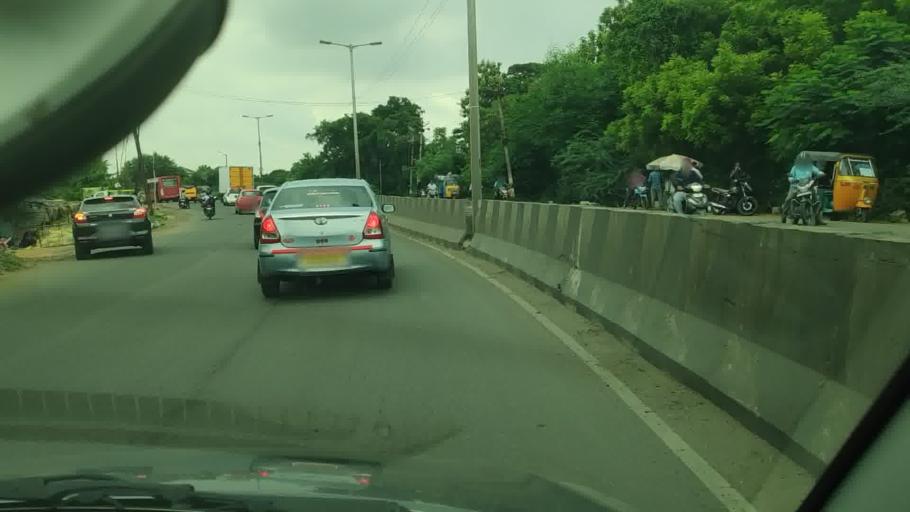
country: IN
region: Tamil Nadu
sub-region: Thiruvallur
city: Ambattur
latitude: 13.1157
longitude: 80.1479
